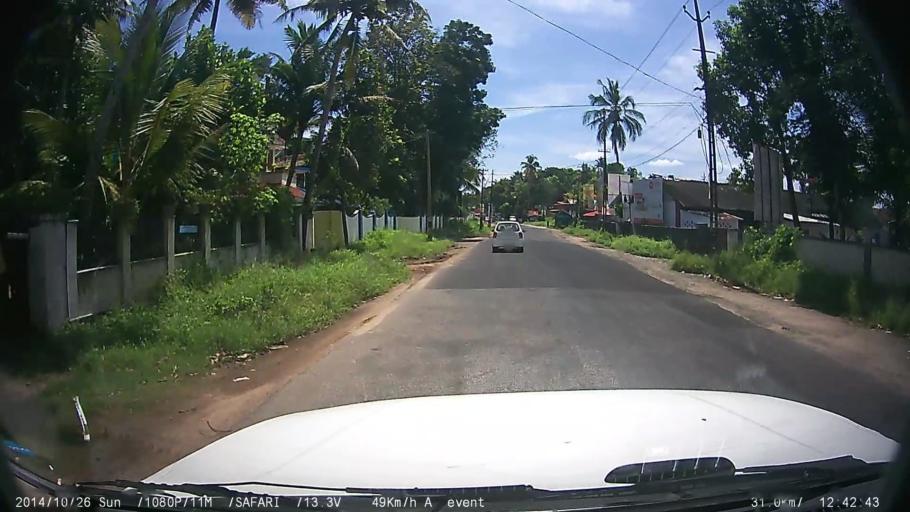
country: IN
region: Kerala
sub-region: Kottayam
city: Kottayam
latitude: 9.5409
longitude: 76.5139
